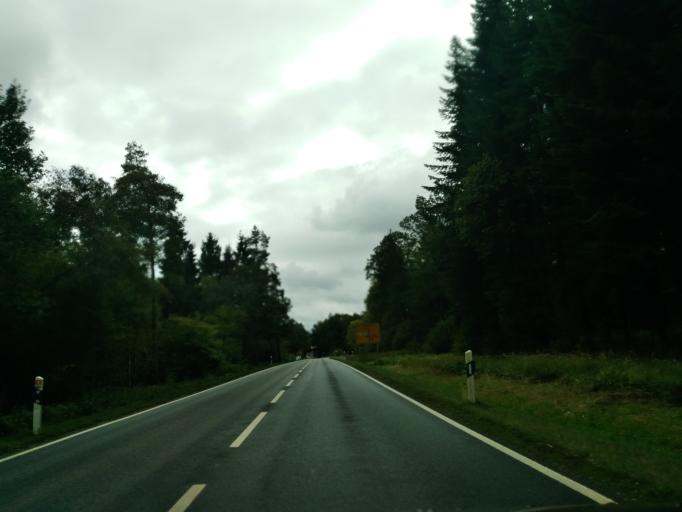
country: DE
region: Rheinland-Pfalz
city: Vettelschoss
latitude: 50.6214
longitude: 7.3085
